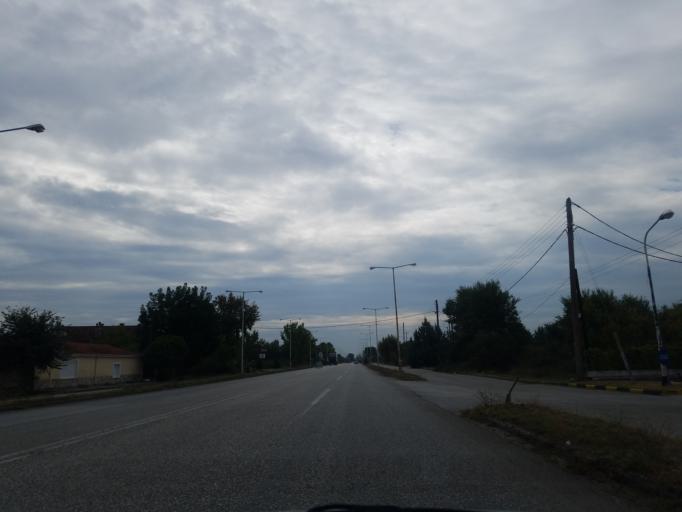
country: GR
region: Thessaly
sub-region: Trikala
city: Pyrgetos
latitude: 39.5806
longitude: 21.7418
